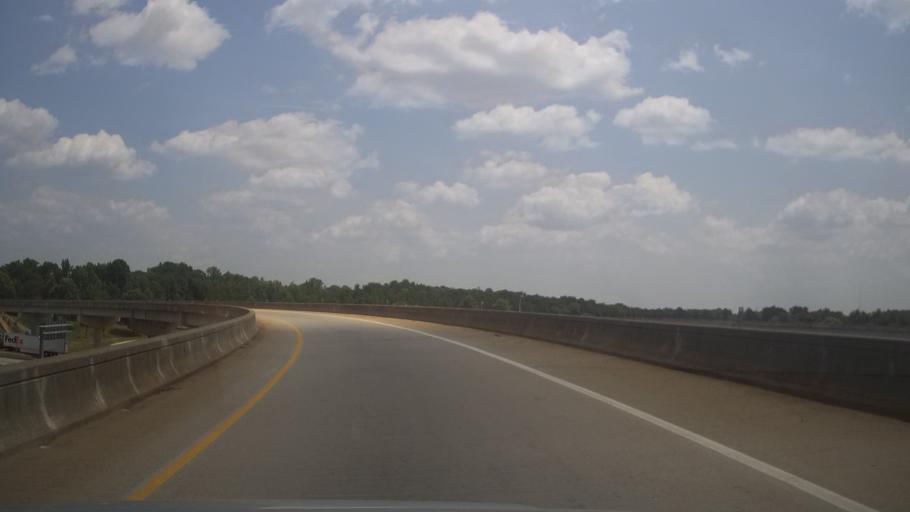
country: US
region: South Carolina
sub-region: Spartanburg County
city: Southern Shops
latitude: 34.9774
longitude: -82.0134
